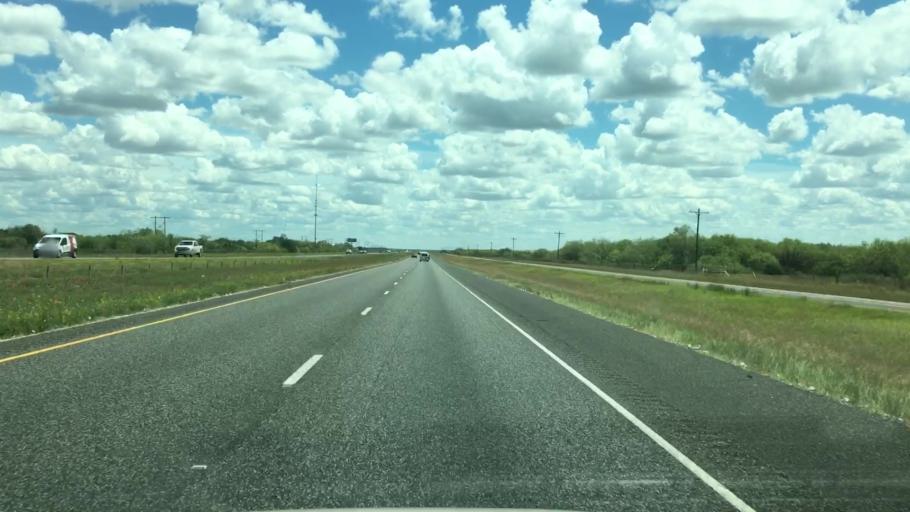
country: US
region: Texas
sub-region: Atascosa County
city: Pleasanton
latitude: 28.8087
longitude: -98.3500
